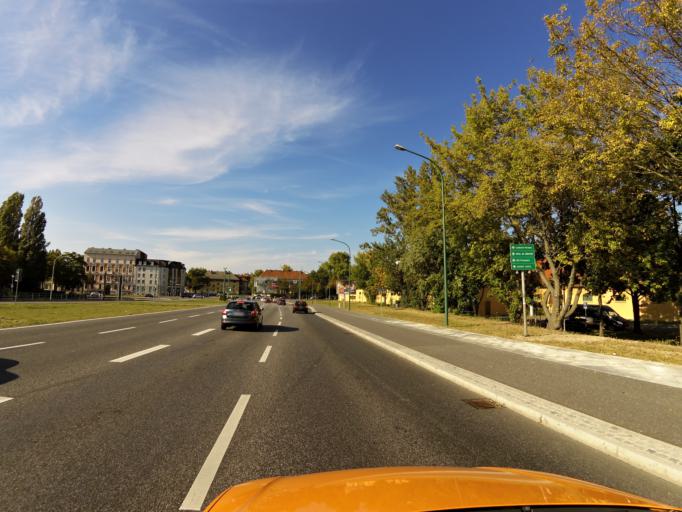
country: DE
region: Brandenburg
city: Potsdam
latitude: 52.4018
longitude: 13.0721
